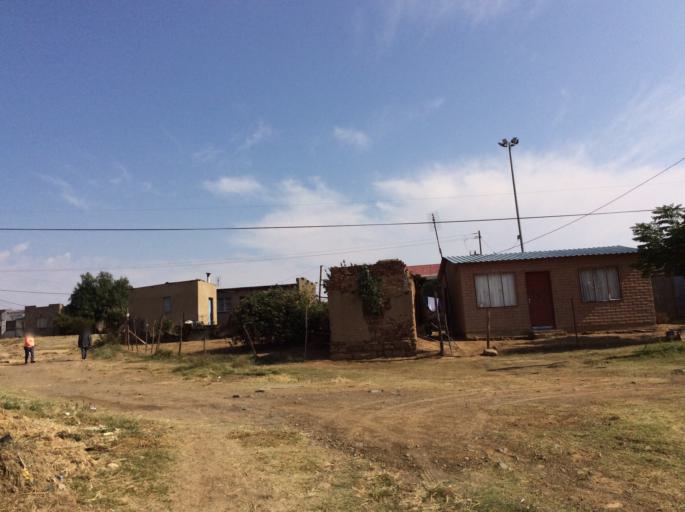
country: LS
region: Mafeteng
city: Mafeteng
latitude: -29.7217
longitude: 27.0339
